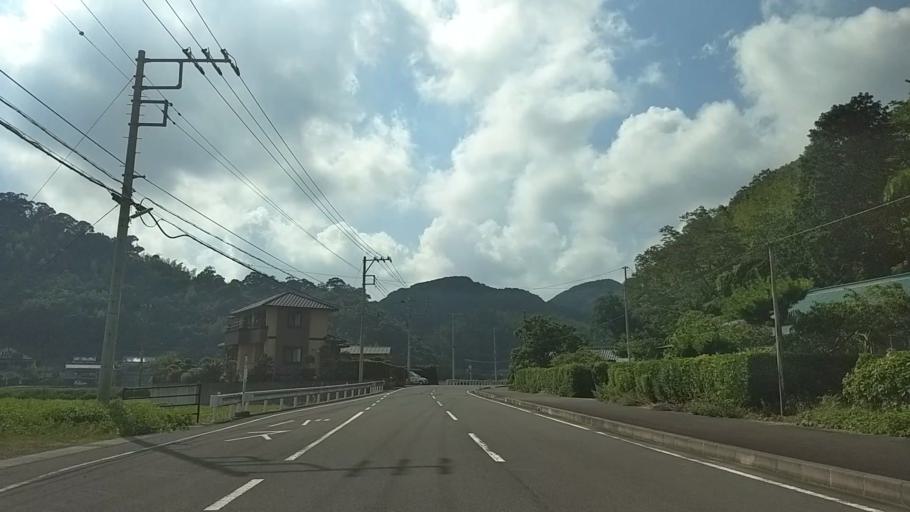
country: JP
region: Shizuoka
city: Shimoda
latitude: 34.6513
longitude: 138.8368
